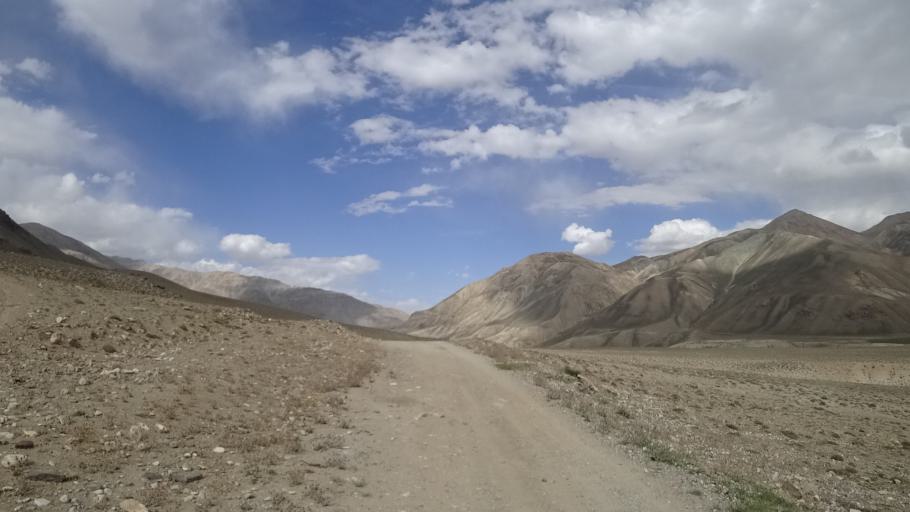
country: AF
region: Badakhshan
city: Khandud
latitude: 37.1929
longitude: 72.7651
